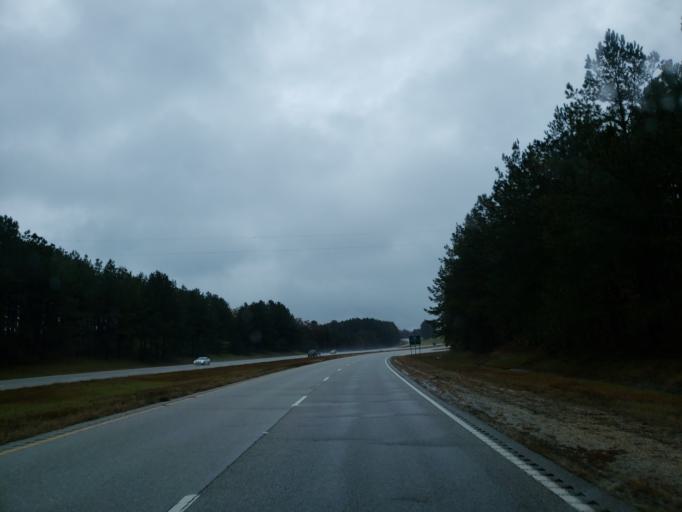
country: US
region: Mississippi
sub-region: Lauderdale County
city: Meridian
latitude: 32.2966
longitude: -88.6948
